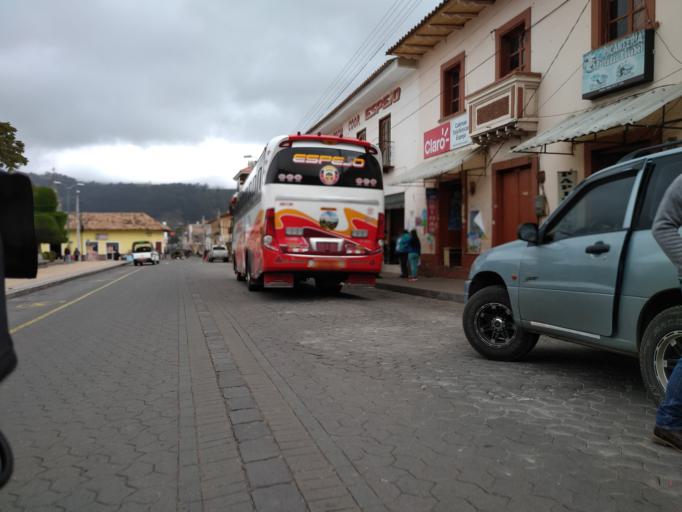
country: EC
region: Carchi
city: El Angel
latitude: 0.6215
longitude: -77.9392
